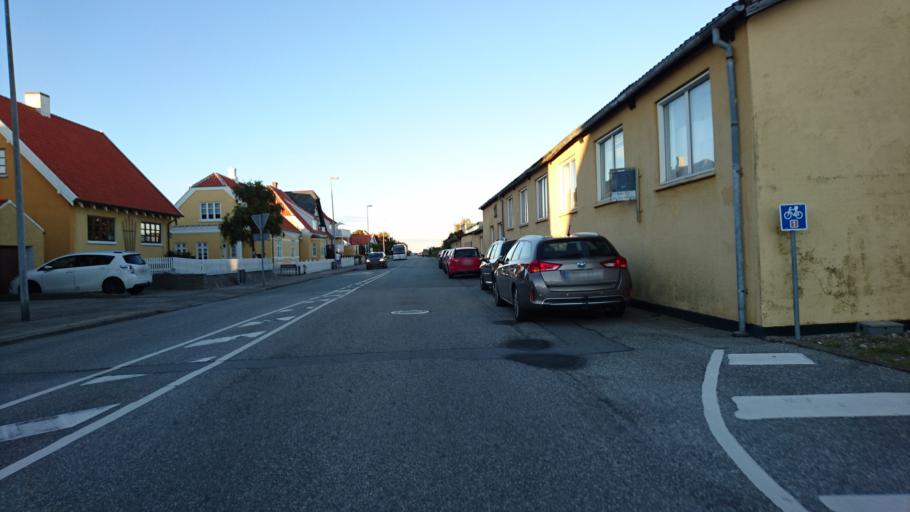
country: DK
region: North Denmark
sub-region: Frederikshavn Kommune
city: Skagen
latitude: 57.7218
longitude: 10.5938
